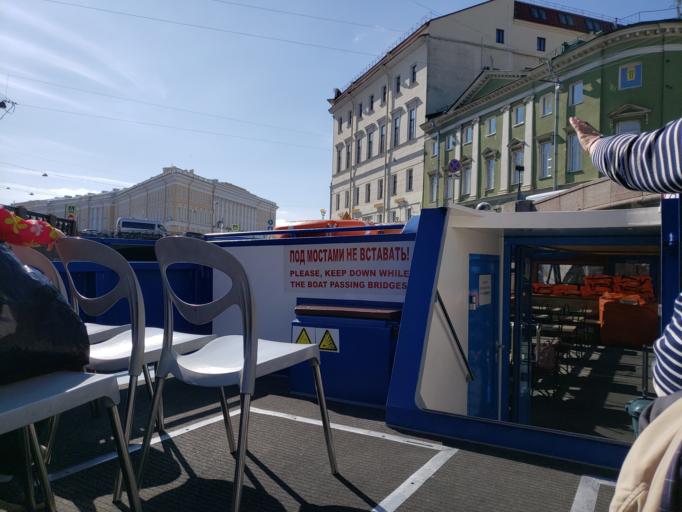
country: RU
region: St.-Petersburg
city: Saint Petersburg
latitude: 59.9410
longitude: 30.3220
